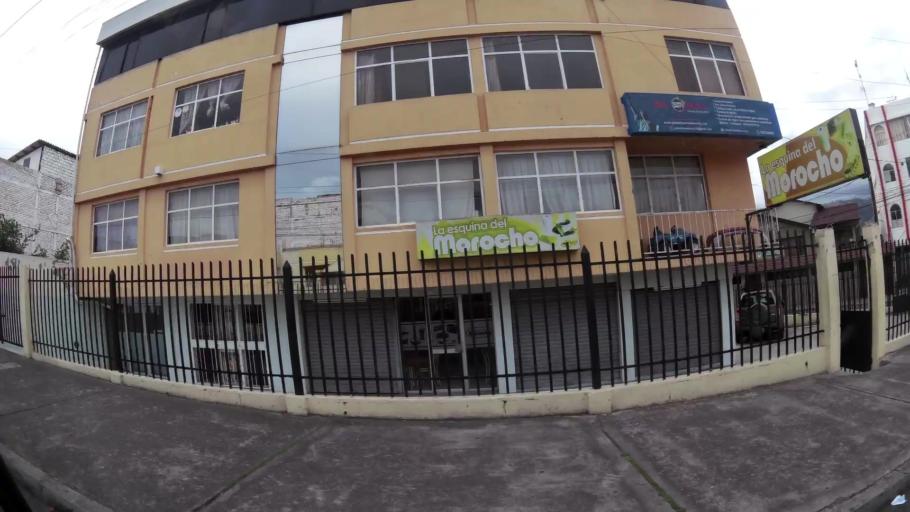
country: EC
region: Tungurahua
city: Ambato
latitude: -1.2576
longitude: -78.6288
